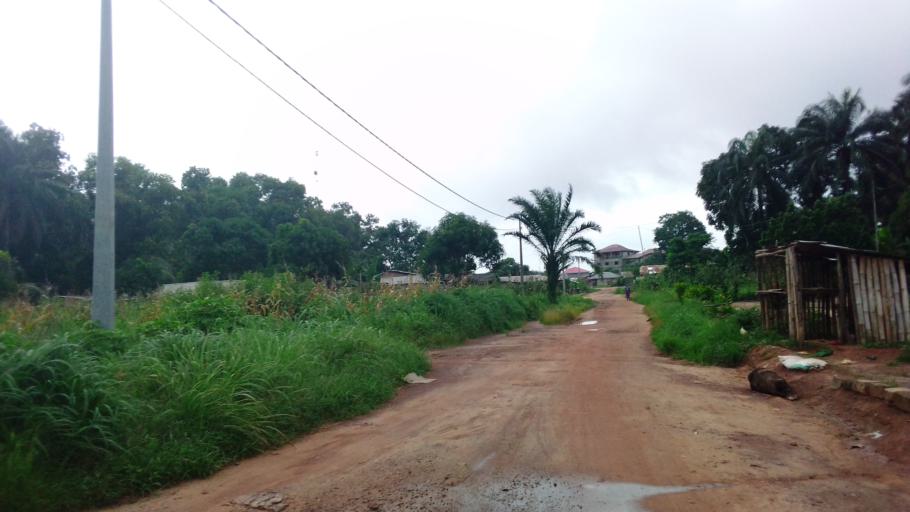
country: SL
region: Northern Province
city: Lunsar
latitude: 8.6893
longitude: -12.5452
